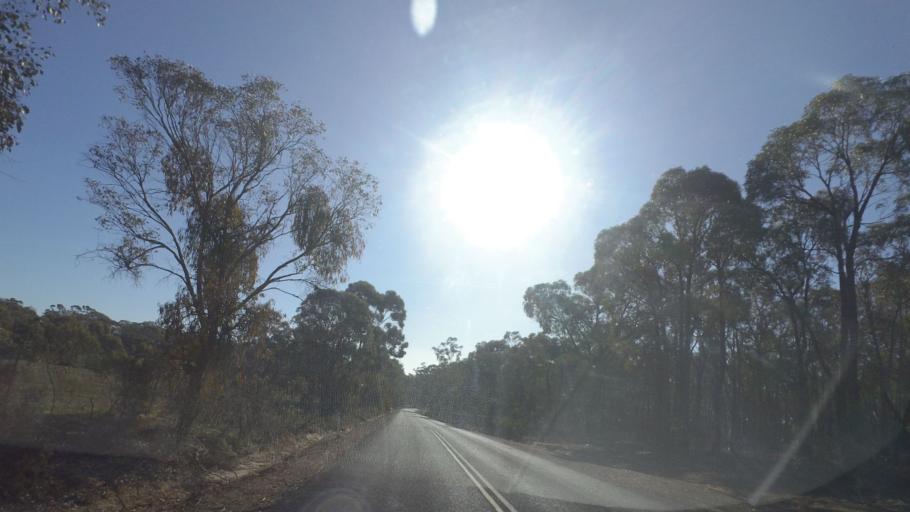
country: AU
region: Victoria
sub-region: Greater Bendigo
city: Kangaroo Flat
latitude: -36.8660
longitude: 144.2842
